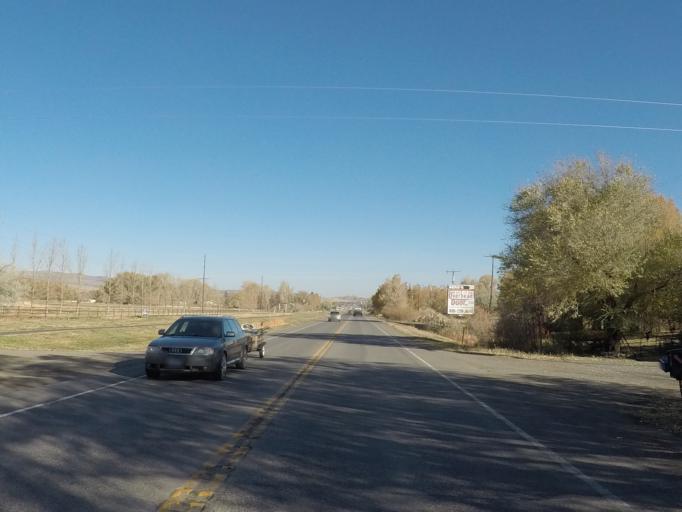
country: US
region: Montana
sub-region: Park County
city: Livingston
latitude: 45.6239
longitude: -110.5781
